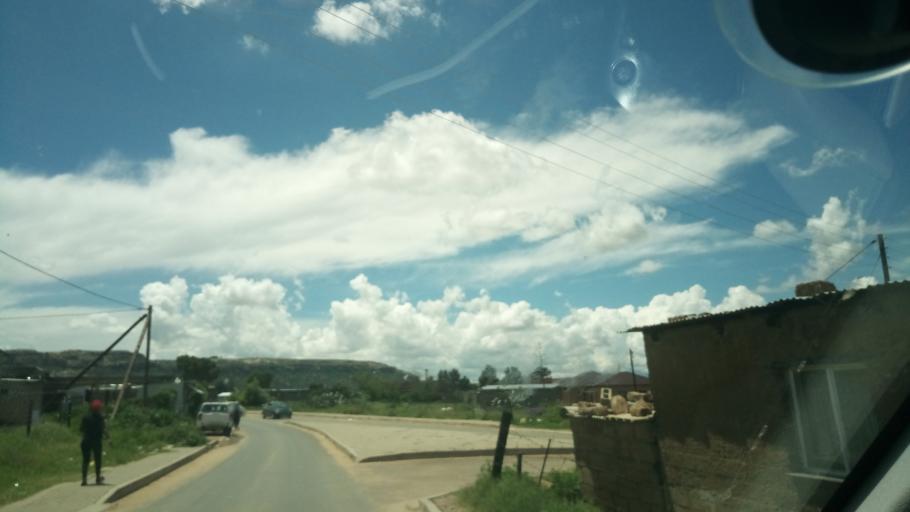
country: LS
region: Maseru
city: Maseru
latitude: -29.3679
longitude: 27.5396
